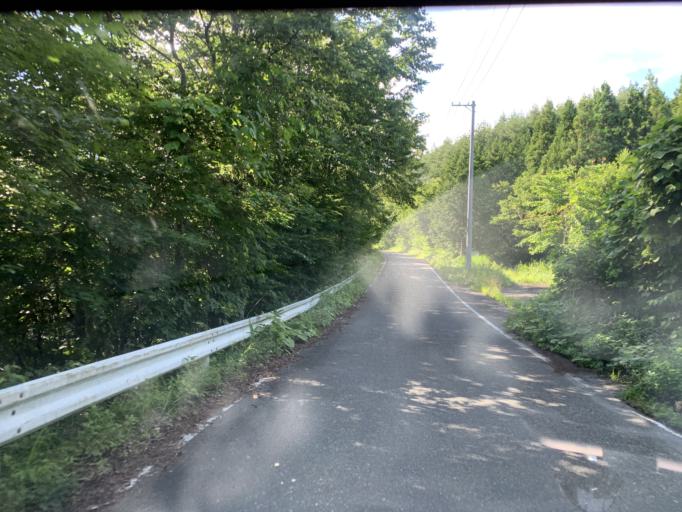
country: JP
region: Iwate
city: Ichinoseki
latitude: 38.8992
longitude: 140.8814
